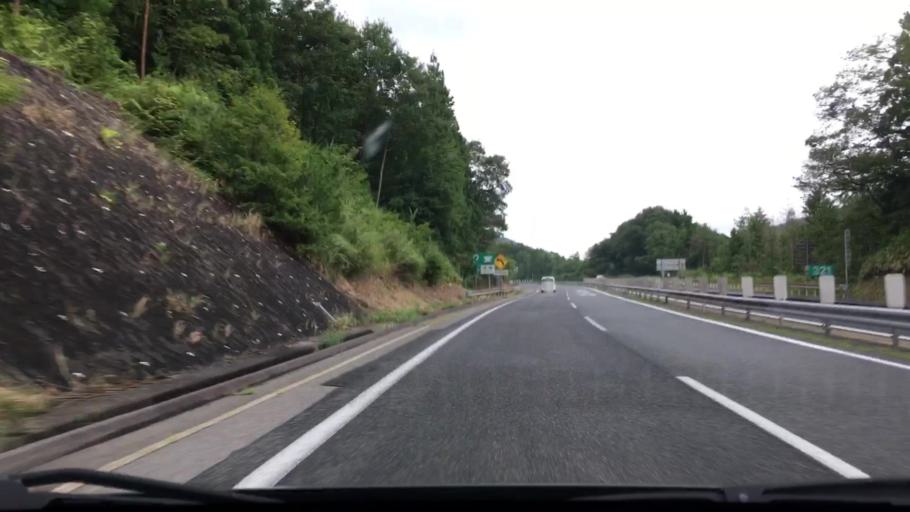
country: JP
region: Hiroshima
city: Miyoshi
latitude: 34.7030
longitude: 132.6110
